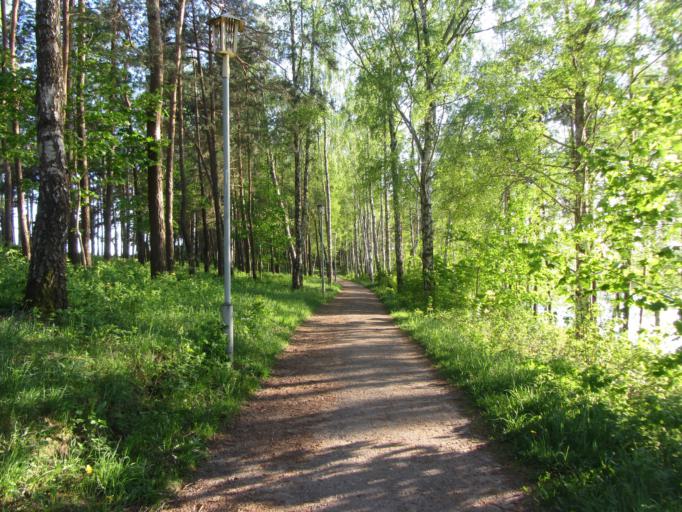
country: LT
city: Moletai
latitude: 55.2290
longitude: 25.4196
